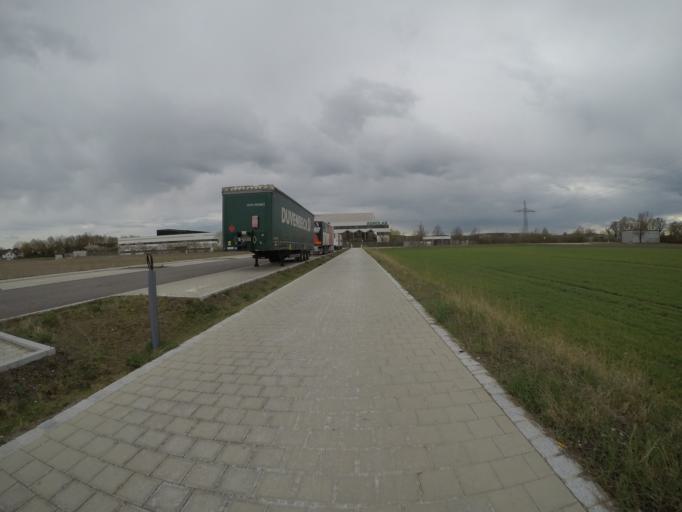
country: DE
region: Bavaria
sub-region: Lower Bavaria
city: Tiefenbach
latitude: 48.5450
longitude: 12.1108
